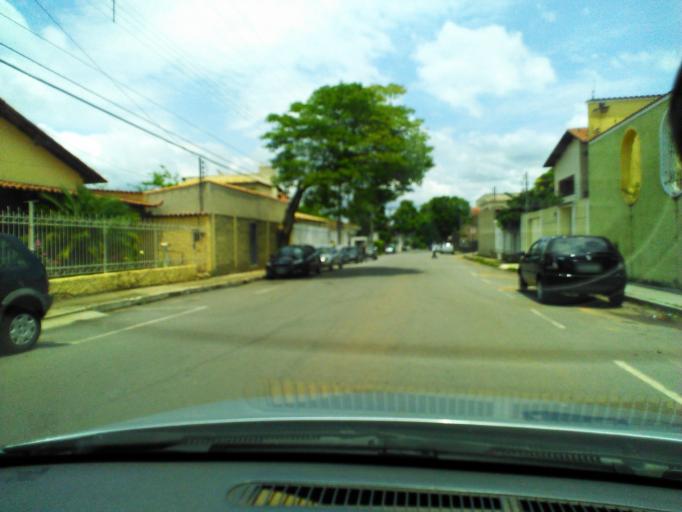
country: BR
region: Minas Gerais
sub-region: Tres Coracoes
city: Tres Coracoes
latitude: -21.6939
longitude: -45.2607
